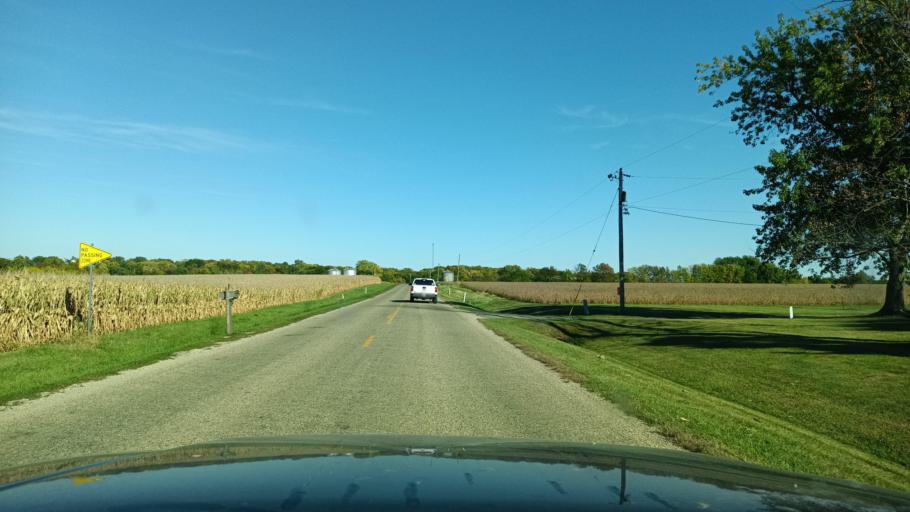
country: US
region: Illinois
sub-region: Logan County
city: Atlanta
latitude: 40.2345
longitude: -89.1381
